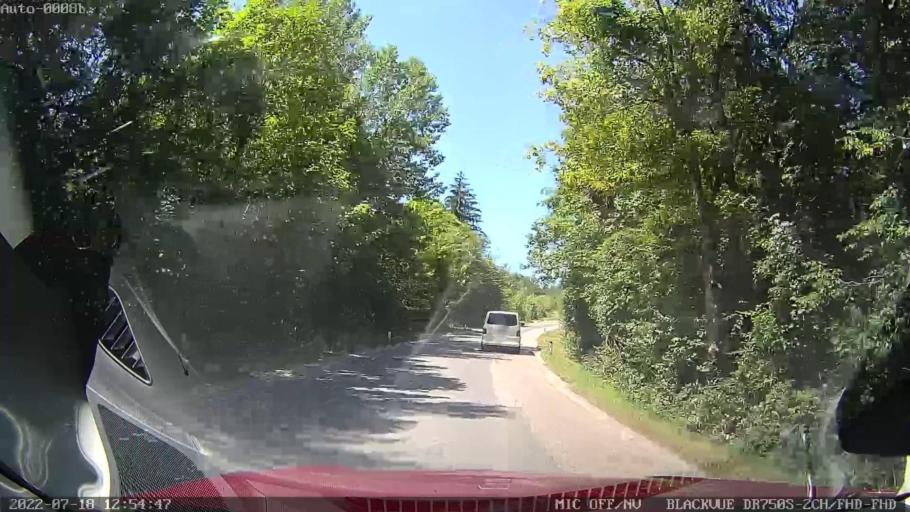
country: SI
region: Dobrova-Horjul-Polhov Gradec
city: Dobrova
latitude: 46.0760
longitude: 14.4389
